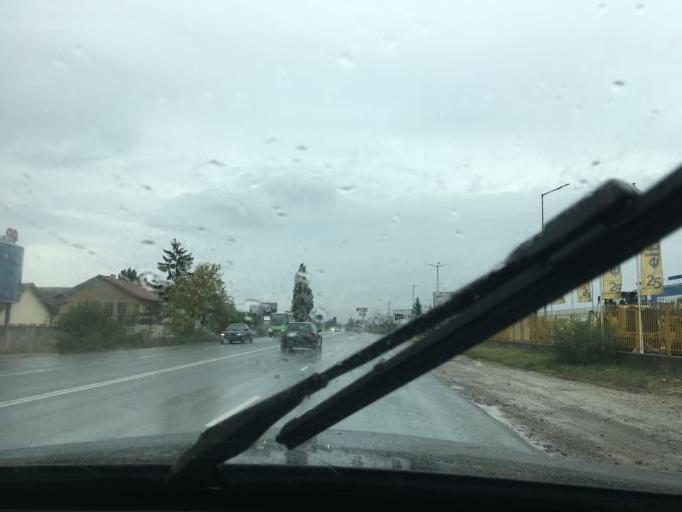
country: BG
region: Sofiya
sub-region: Obshtina Bozhurishte
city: Bozhurishte
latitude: 42.7438
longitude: 23.2313
